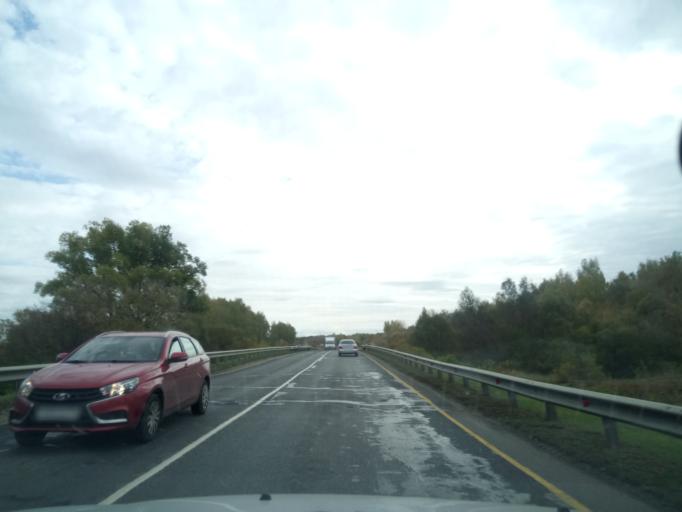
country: RU
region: Nizjnij Novgorod
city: Lukoyanov
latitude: 55.0557
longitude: 44.3691
